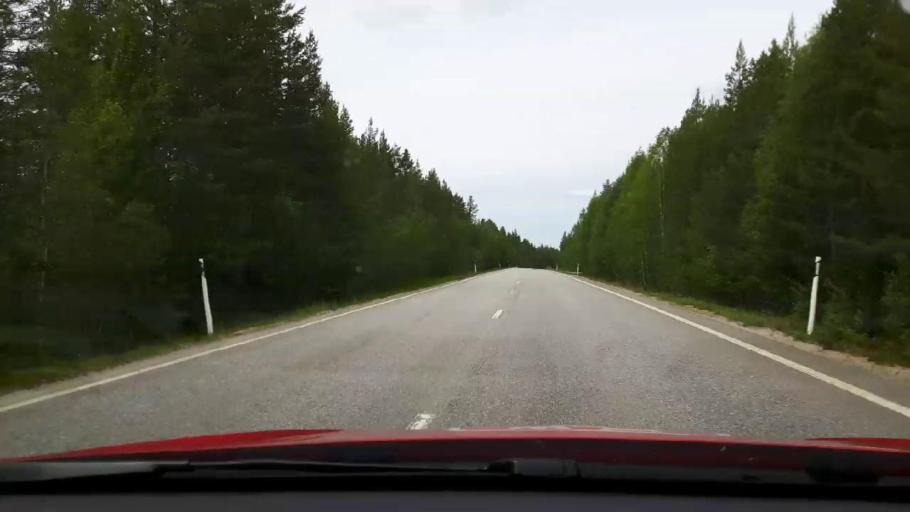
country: SE
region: Jaemtland
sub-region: Harjedalens Kommun
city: Sveg
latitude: 62.0783
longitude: 14.2631
